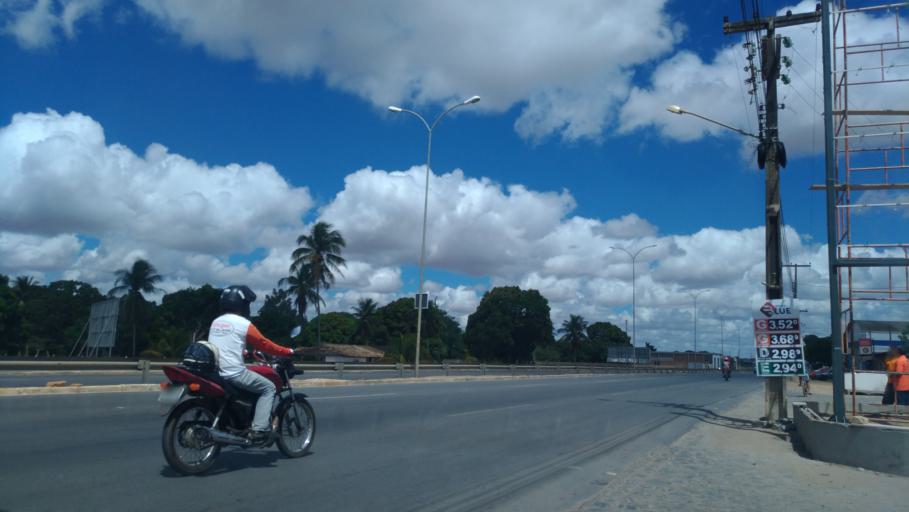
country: BR
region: Alagoas
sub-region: Arapiraca
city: Arapiraca
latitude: -9.7291
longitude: -36.6644
